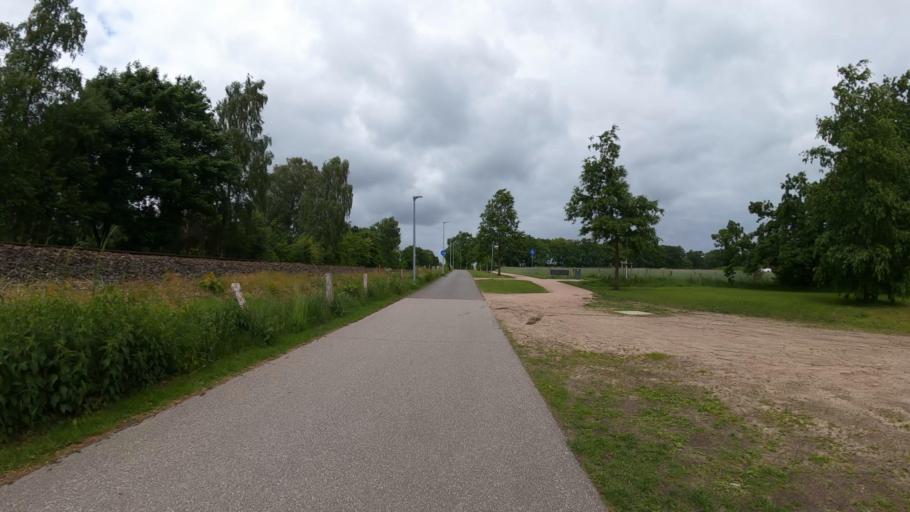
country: DE
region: Schleswig-Holstein
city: Norderstedt
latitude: 53.7190
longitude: 9.9918
